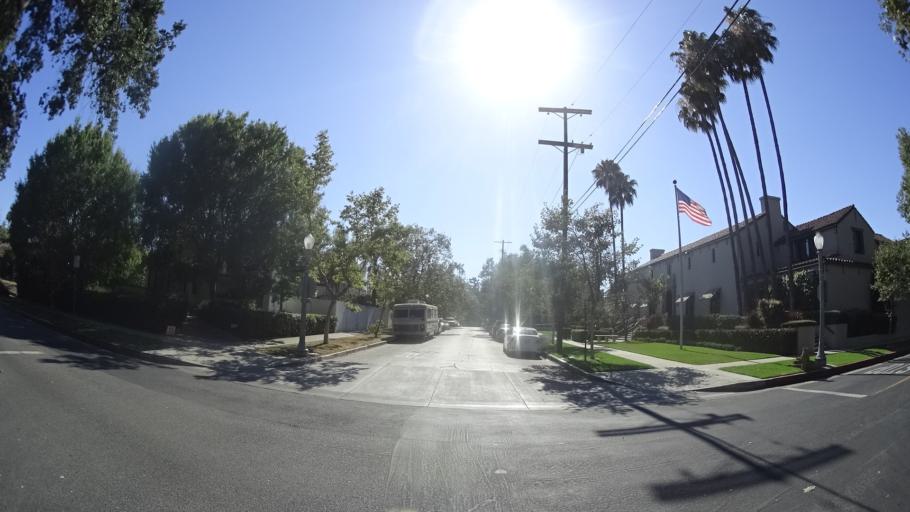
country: US
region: California
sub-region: Los Angeles County
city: Hollywood
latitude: 34.0817
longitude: -118.3294
